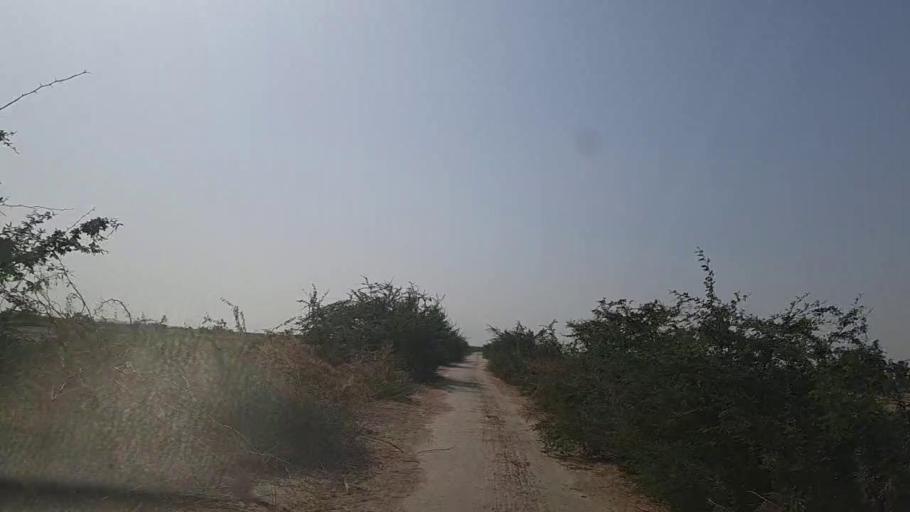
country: PK
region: Sindh
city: Naukot
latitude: 24.5689
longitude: 69.2859
